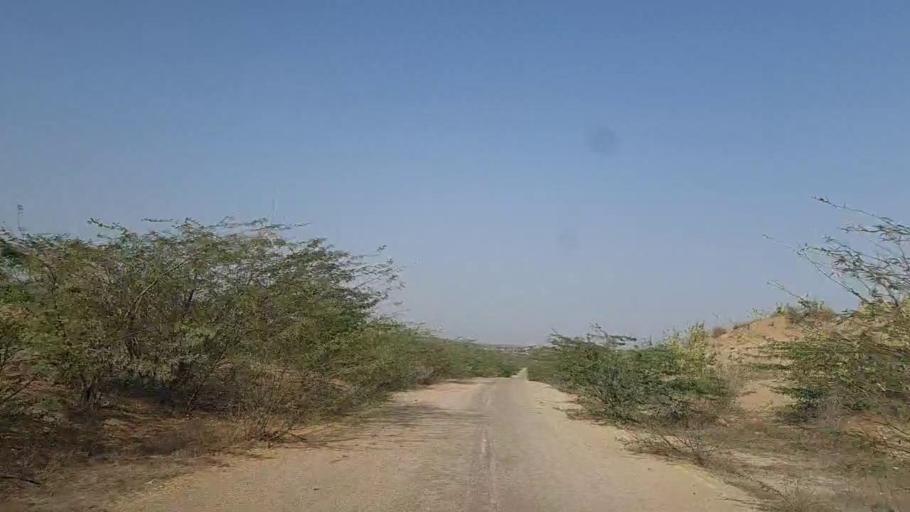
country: PK
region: Sindh
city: Naukot
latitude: 24.6238
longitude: 69.3522
